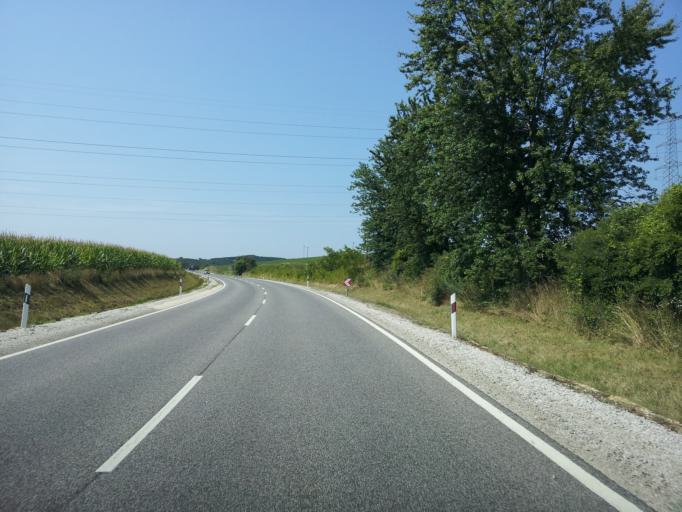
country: HU
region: Zala
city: Pacsa
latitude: 46.8306
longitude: 17.0185
